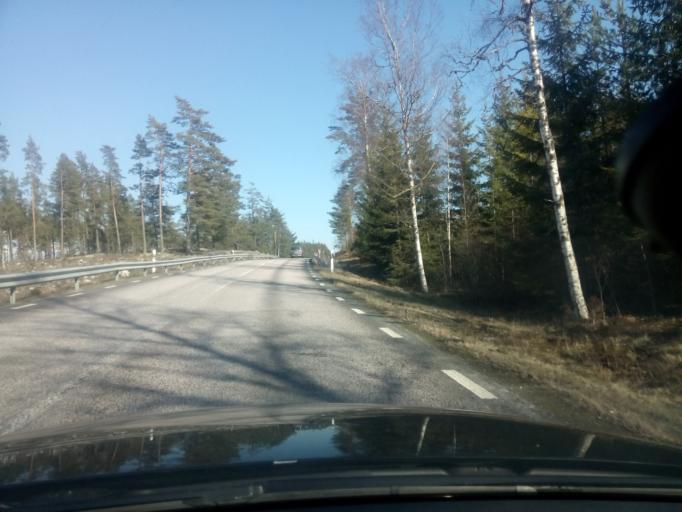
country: SE
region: Soedermanland
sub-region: Flens Kommun
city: Malmkoping
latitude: 59.2063
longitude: 16.8003
